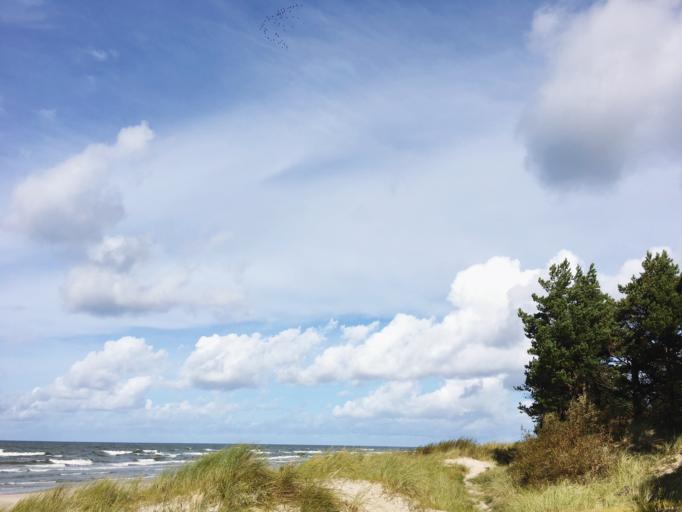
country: LT
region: Klaipedos apskritis
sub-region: Klaipeda
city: Palanga
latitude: 55.9004
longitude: 21.0513
